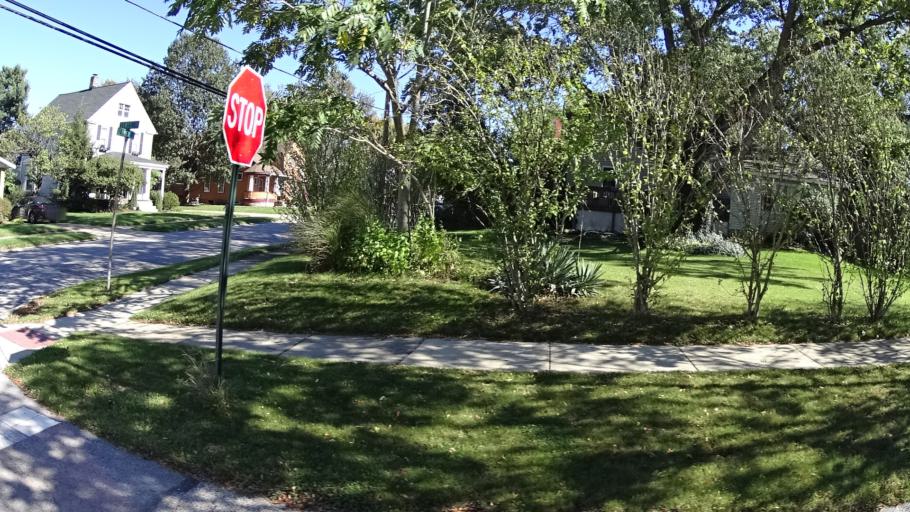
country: US
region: Ohio
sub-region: Lorain County
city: Amherst
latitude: 41.3971
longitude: -82.2189
